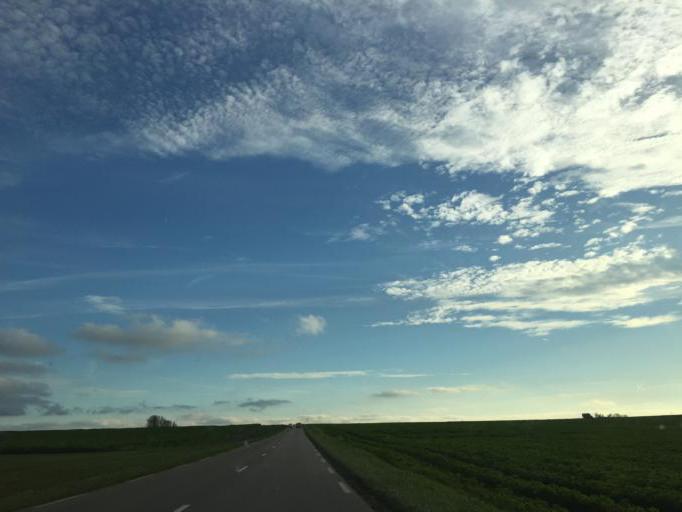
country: FR
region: Ile-de-France
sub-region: Departement de Seine-et-Marne
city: Jouy-le-Chatel
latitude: 48.6436
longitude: 3.1029
